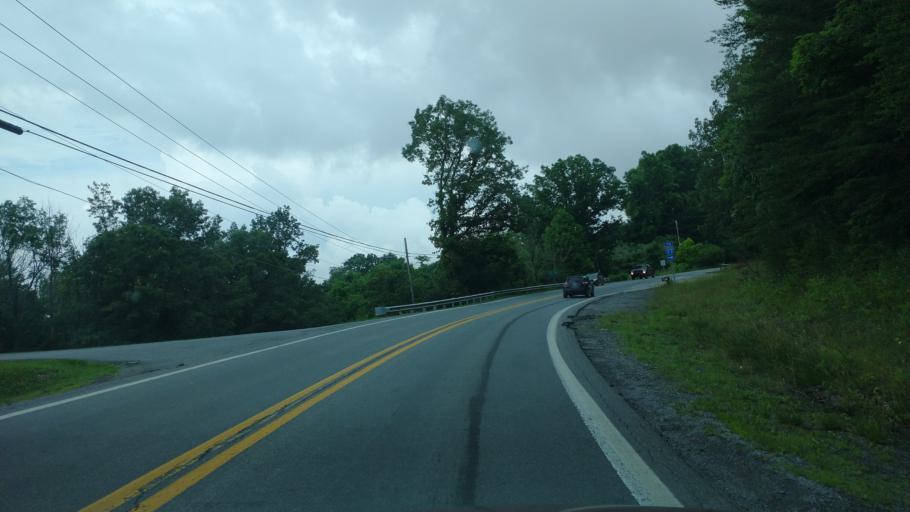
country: US
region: West Virginia
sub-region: Mercer County
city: Athens
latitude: 37.4065
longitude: -81.0316
